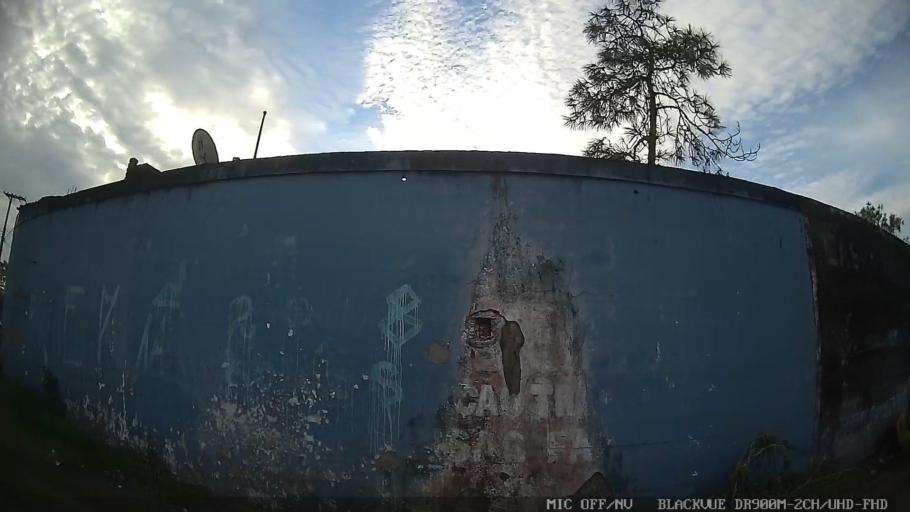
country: BR
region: Sao Paulo
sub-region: Itanhaem
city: Itanhaem
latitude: -24.1679
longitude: -46.7778
